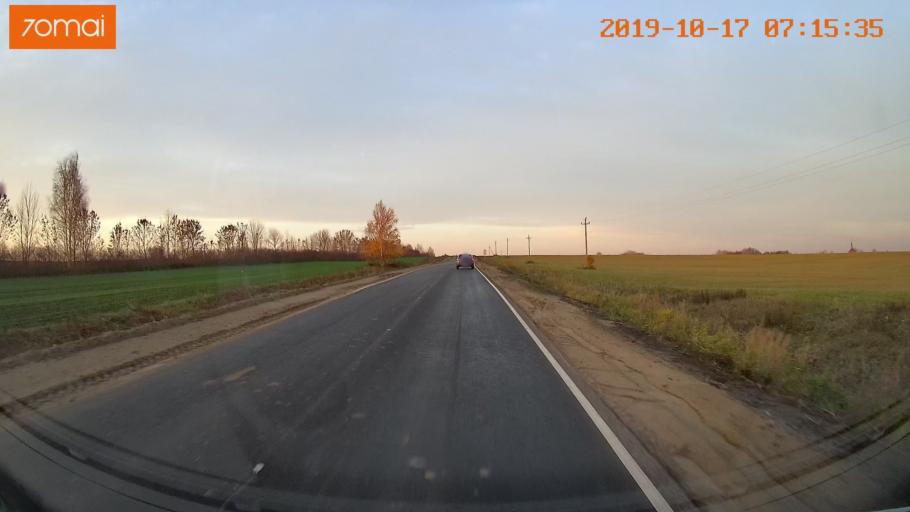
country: RU
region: Vladimir
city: Suzdal'
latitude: 56.3791
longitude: 40.2649
